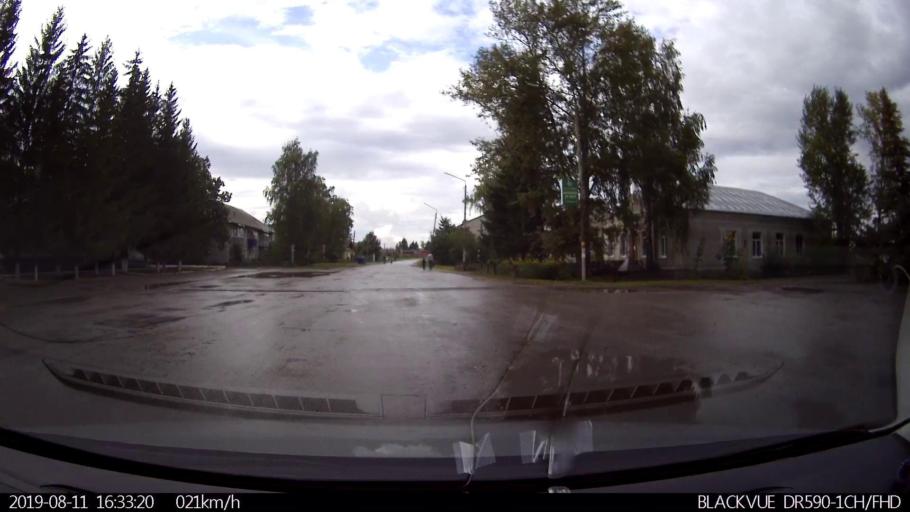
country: RU
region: Ulyanovsk
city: Mayna
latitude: 54.1143
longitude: 47.6260
